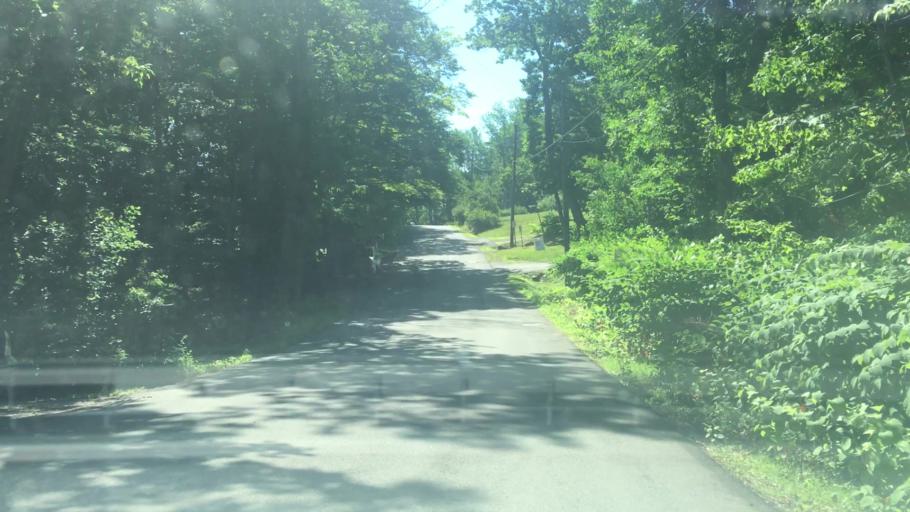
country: US
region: Maine
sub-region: Waldo County
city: Northport
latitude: 44.3782
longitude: -68.9672
